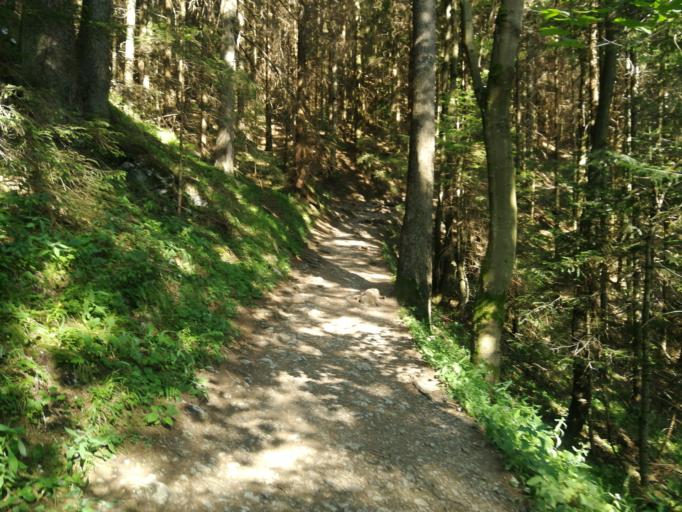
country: SK
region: Zilinsky
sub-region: Okres Liptovsky Mikulas
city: Liptovsky Mikulas
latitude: 49.1963
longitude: 19.5423
